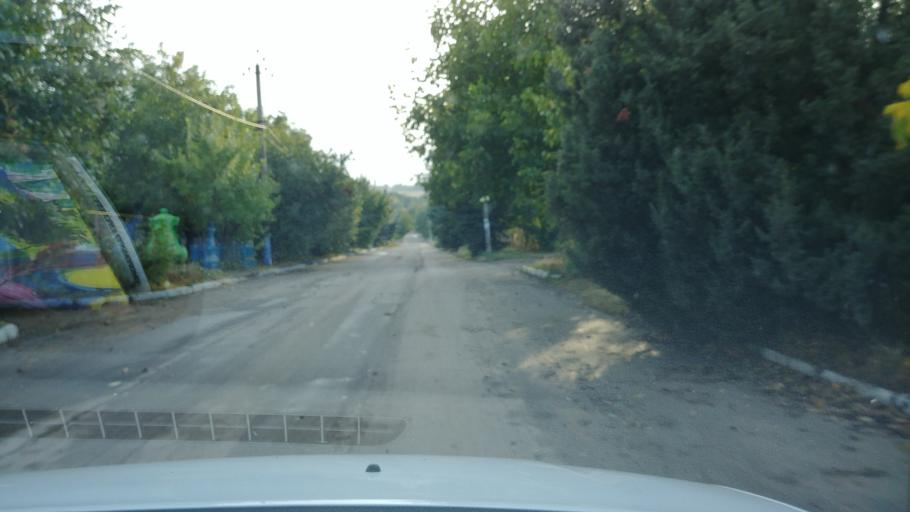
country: MD
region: Rezina
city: Saharna
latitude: 47.6775
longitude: 28.9637
